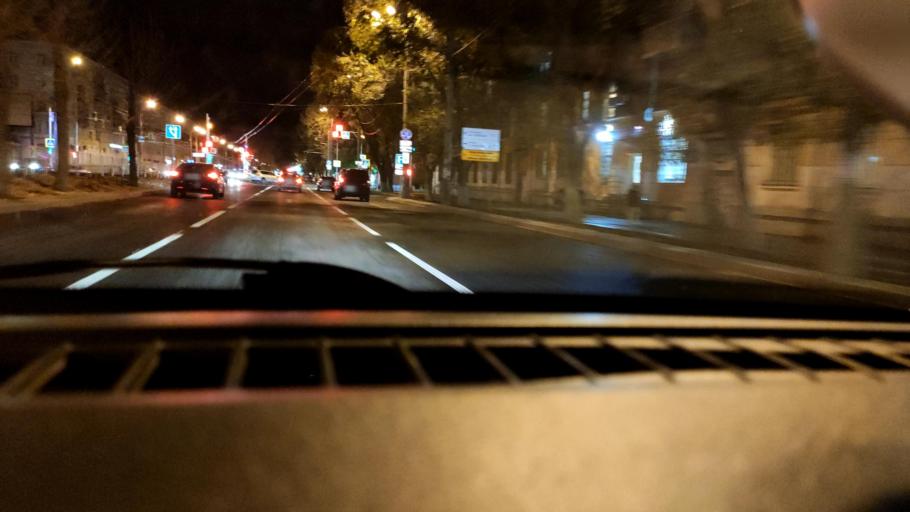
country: RU
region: Samara
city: Samara
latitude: 53.2100
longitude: 50.2426
